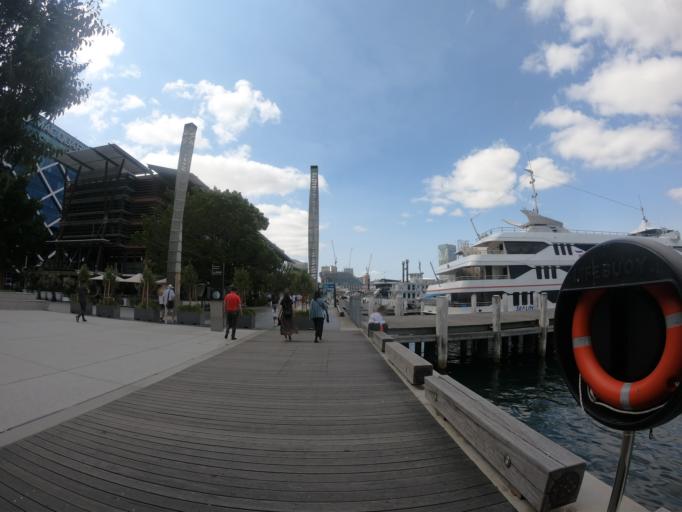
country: AU
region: New South Wales
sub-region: City of Sydney
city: Sydney
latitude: -33.8657
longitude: 151.2012
